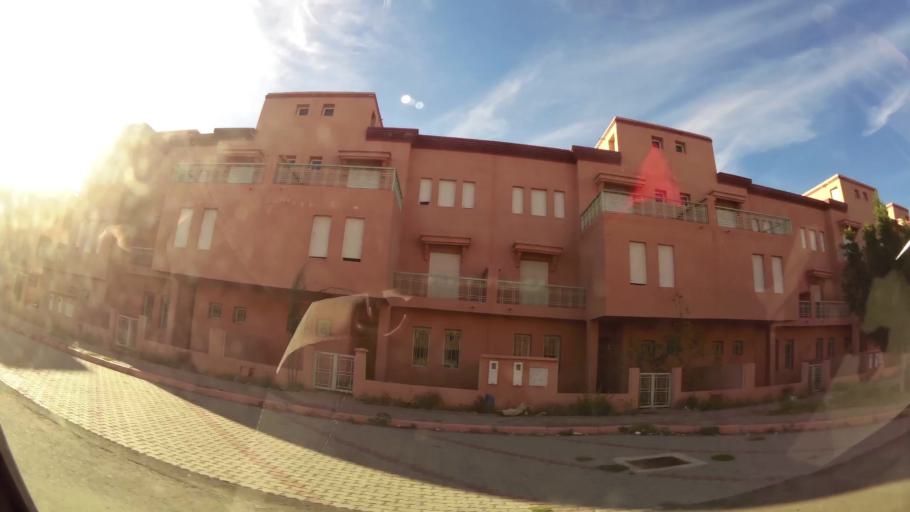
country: MA
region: Marrakech-Tensift-Al Haouz
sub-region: Marrakech
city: Marrakesh
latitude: 31.7601
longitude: -8.0987
